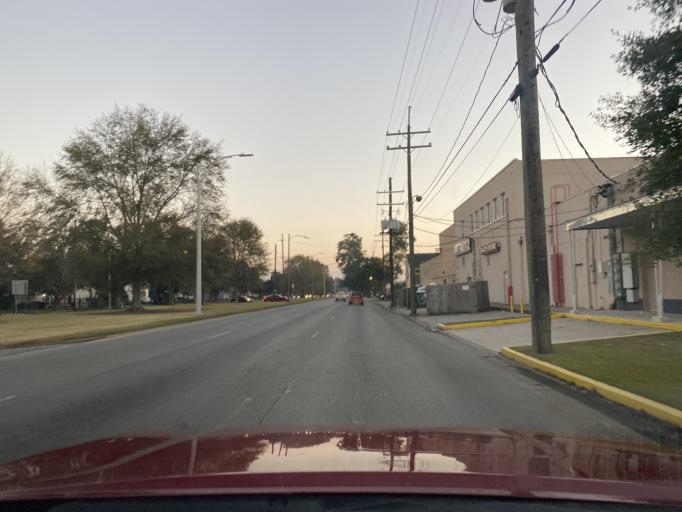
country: US
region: Louisiana
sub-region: Orleans Parish
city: New Orleans
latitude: 29.9988
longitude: -90.0594
